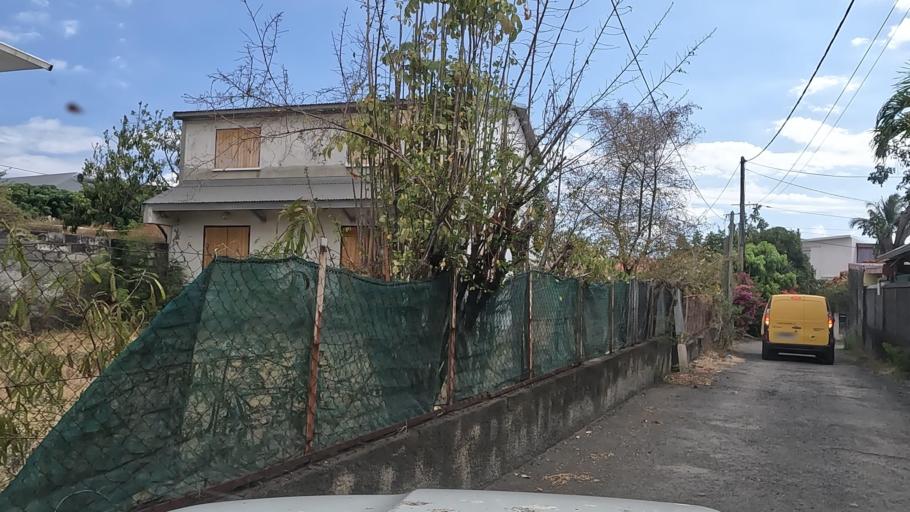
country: RE
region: Reunion
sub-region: Reunion
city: Saint-Louis
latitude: -21.2866
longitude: 55.4142
